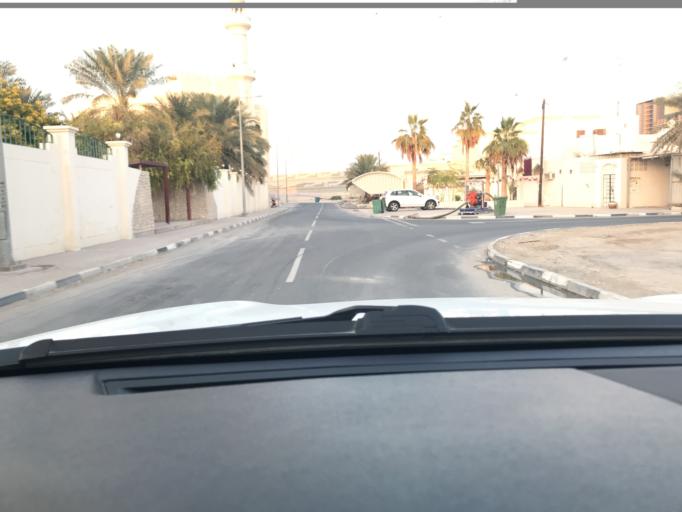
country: QA
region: Baladiyat ad Dawhah
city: Doha
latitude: 25.2545
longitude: 51.5036
